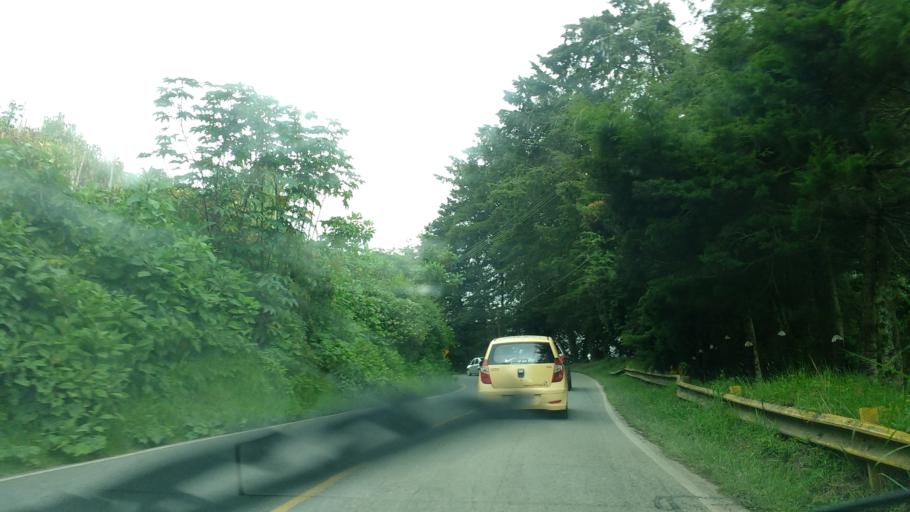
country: CO
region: Antioquia
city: Marinilla
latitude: 6.1766
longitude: -75.3185
